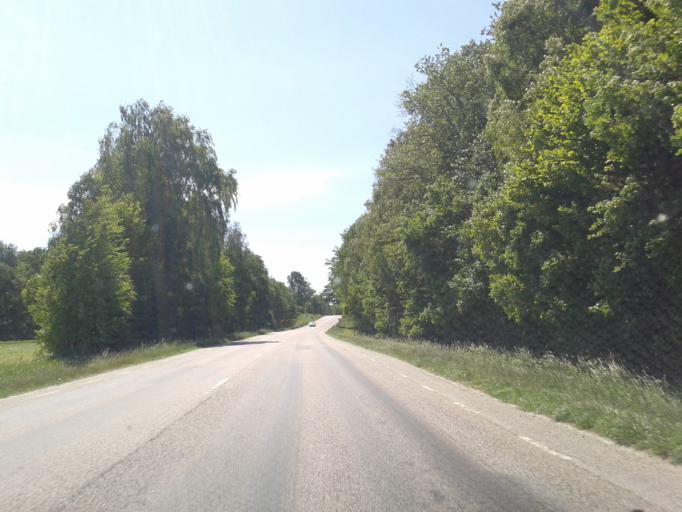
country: SE
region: Vaestra Goetaland
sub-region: Stenungsunds Kommun
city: Stora Hoga
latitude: 58.0690
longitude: 11.9329
